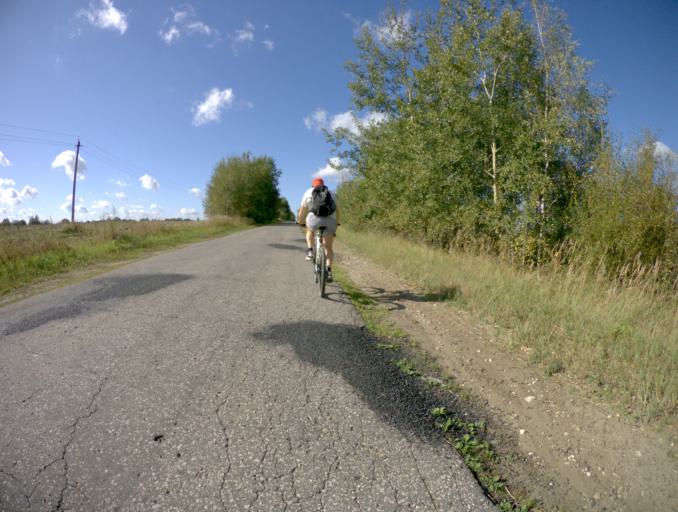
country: RU
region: Vladimir
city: Lakinsk
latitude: 55.8969
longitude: 39.8807
